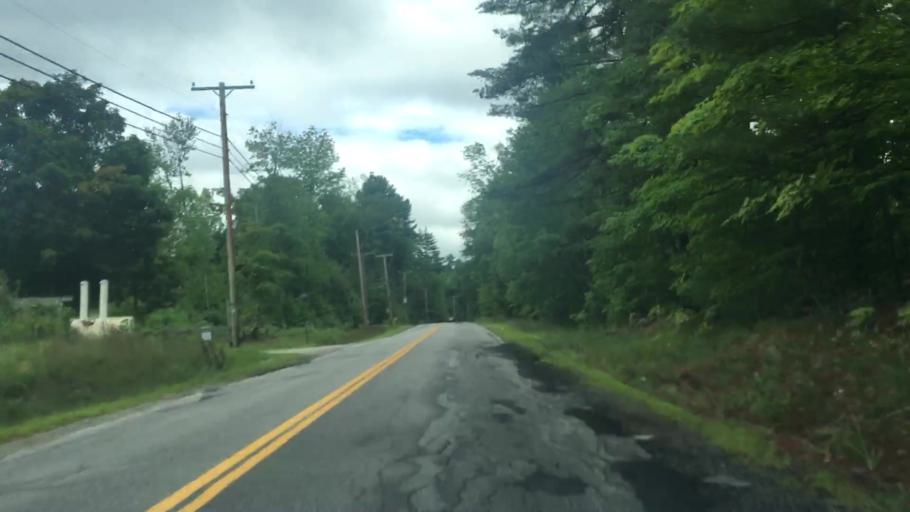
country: US
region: Maine
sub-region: York County
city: Lake Arrowhead
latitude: 43.6626
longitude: -70.7682
